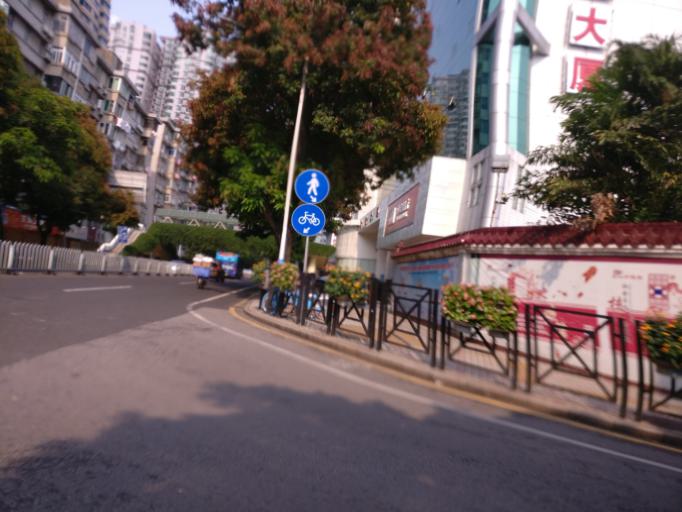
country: CN
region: Guangdong
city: Guangzhou
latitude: 23.1228
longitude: 113.2972
